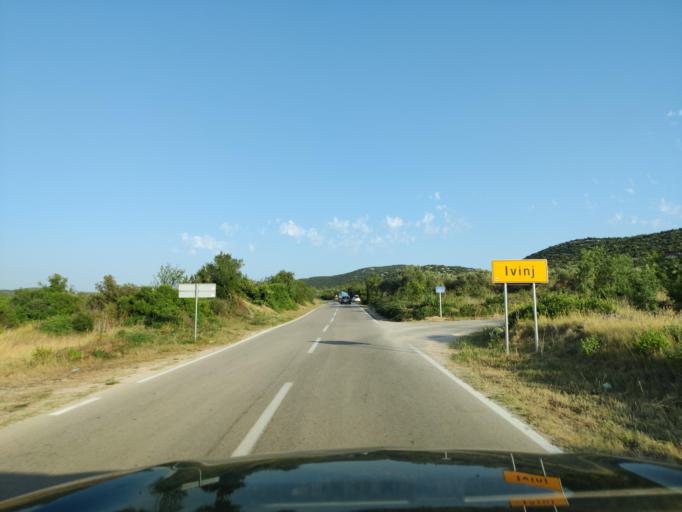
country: HR
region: Sibensko-Kniniska
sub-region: Grad Sibenik
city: Pirovac
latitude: 43.7963
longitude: 15.6826
